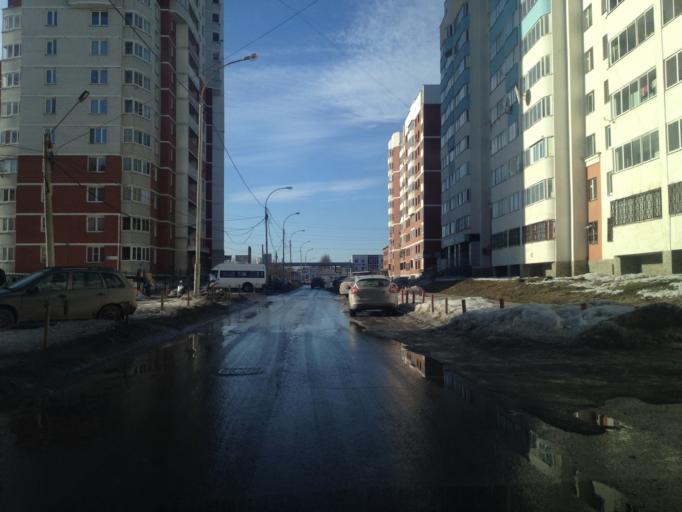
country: RU
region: Sverdlovsk
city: Yekaterinburg
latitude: 56.8727
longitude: 60.5453
